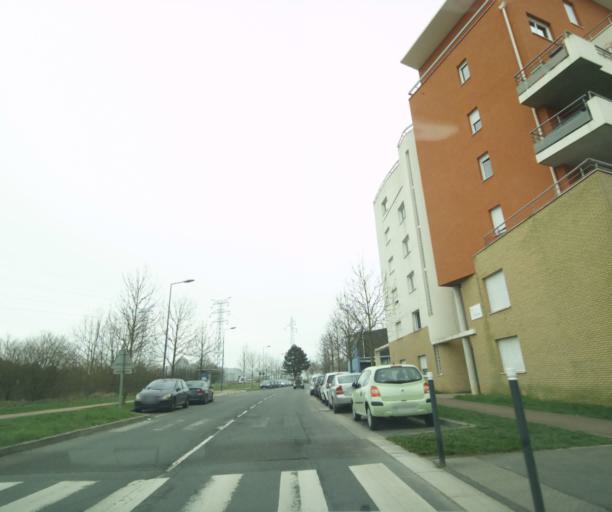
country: FR
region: Ile-de-France
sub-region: Departement du Val-d'Oise
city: Courdimanche
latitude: 49.0523
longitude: 2.0078
